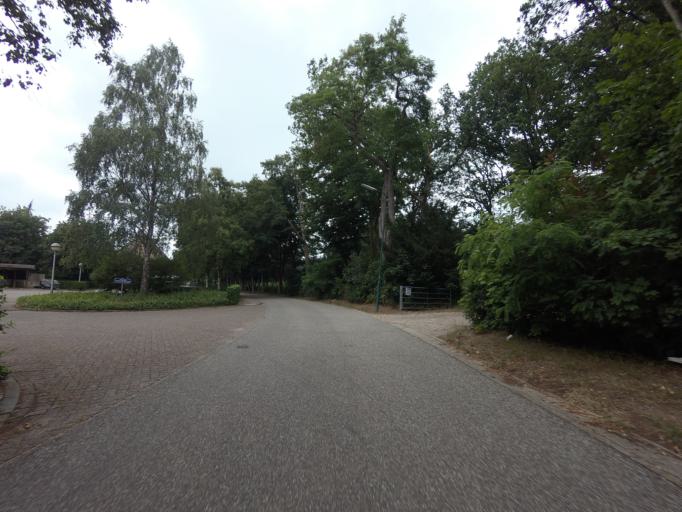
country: NL
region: Utrecht
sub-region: Gemeente Utrechtse Heuvelrug
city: Amerongen
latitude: 52.0074
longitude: 5.4652
